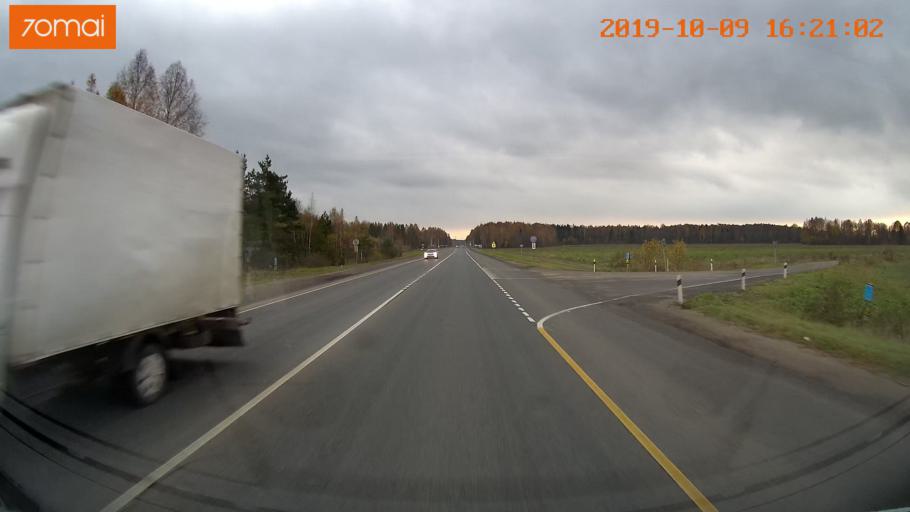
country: RU
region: Kostroma
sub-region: Kostromskoy Rayon
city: Kostroma
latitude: 57.6982
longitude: 40.8905
